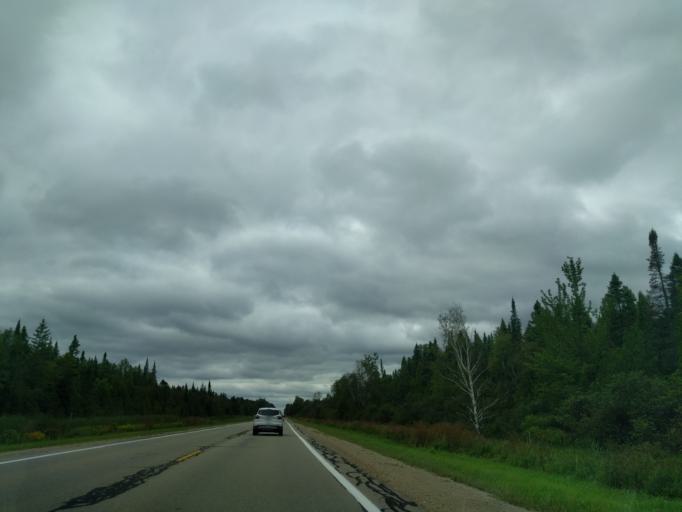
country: US
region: Michigan
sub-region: Menominee County
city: Menominee
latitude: 45.3561
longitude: -87.4015
